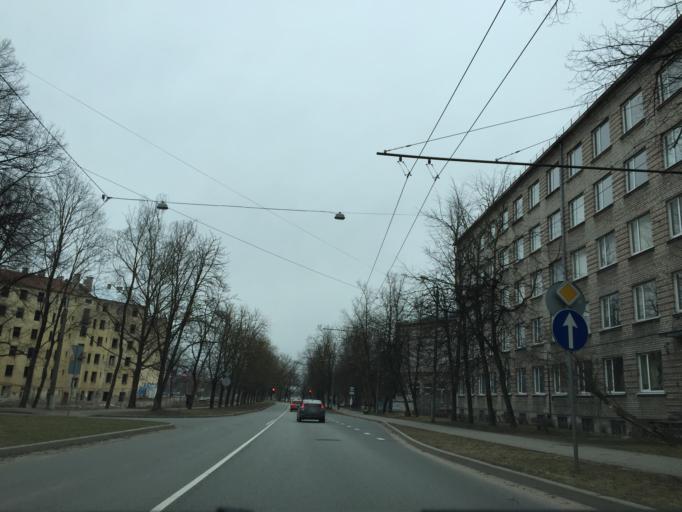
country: LV
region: Riga
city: Riga
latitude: 56.9456
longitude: 24.0807
